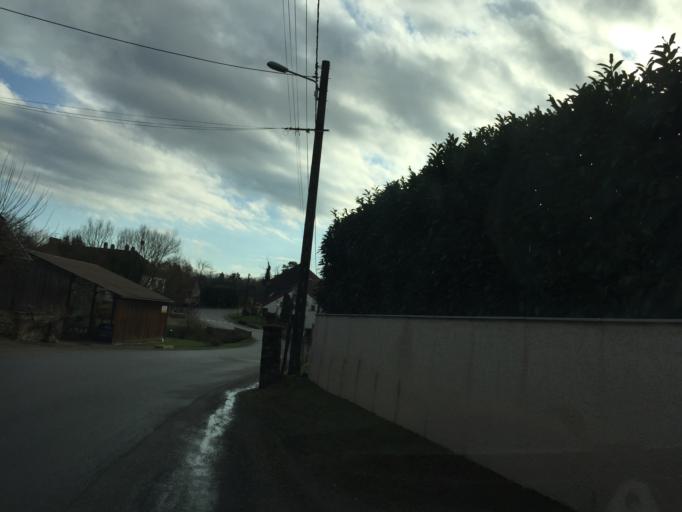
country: FR
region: Franche-Comte
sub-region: Departement du Jura
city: Mont-sous-Vaudrey
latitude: 46.9799
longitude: 5.6222
